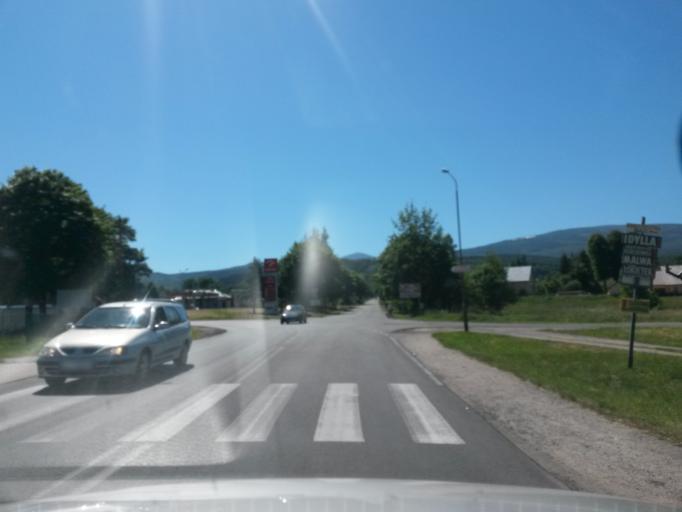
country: PL
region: Lower Silesian Voivodeship
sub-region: Powiat jeleniogorski
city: Podgorzyn
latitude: 50.8338
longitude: 15.6836
